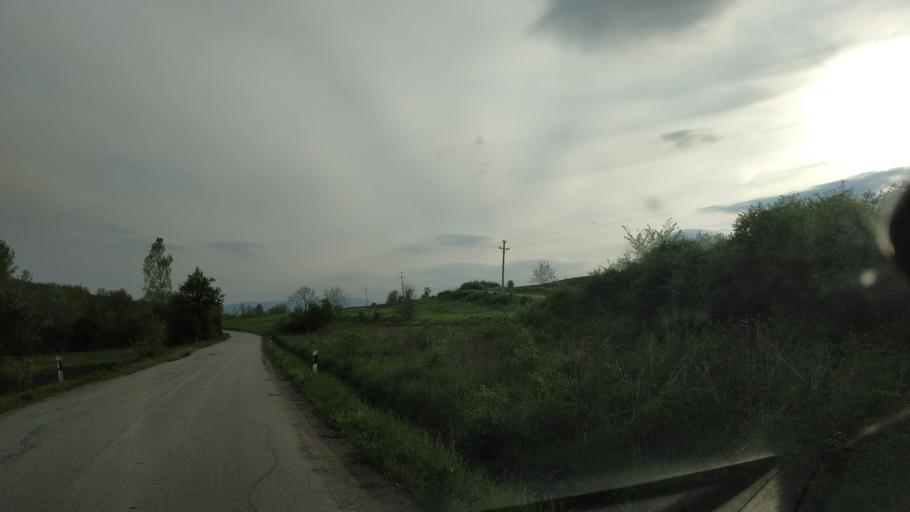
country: RS
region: Central Serbia
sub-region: Nisavski Okrug
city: Aleksinac
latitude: 43.5053
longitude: 21.8413
